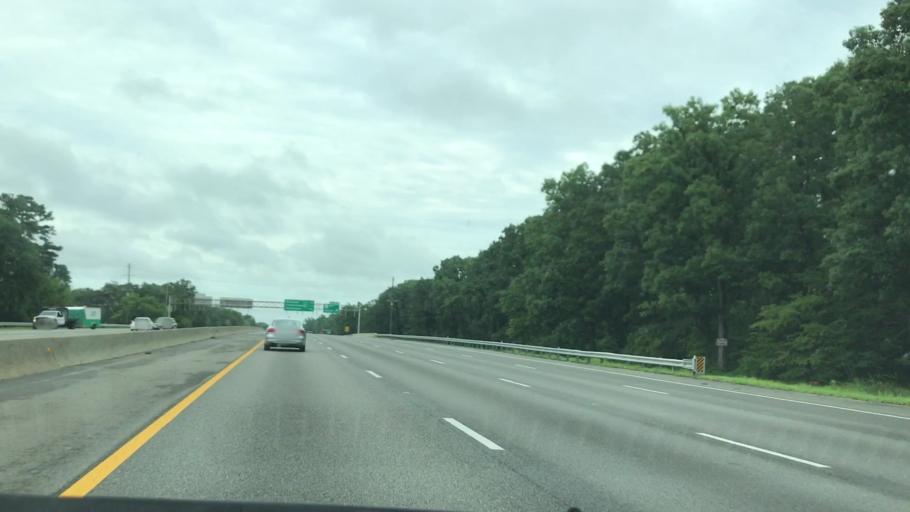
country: US
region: Virginia
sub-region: Chesterfield County
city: Chester
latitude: 37.3528
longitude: -77.4047
